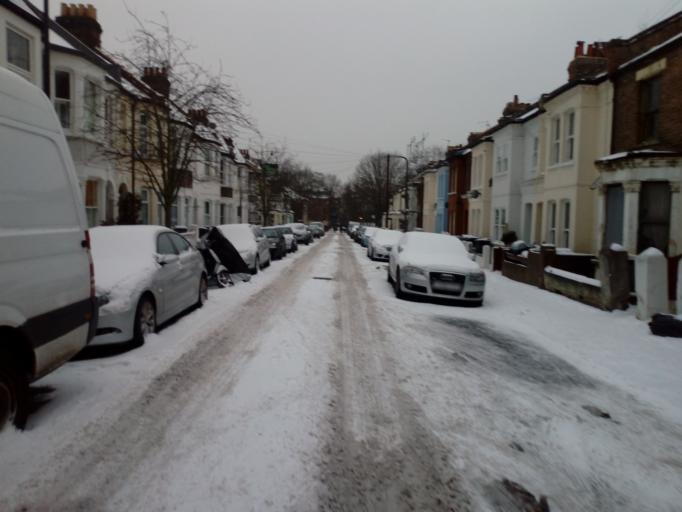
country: GB
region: England
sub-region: Greater London
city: Hammersmith
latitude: 51.5317
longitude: -0.2278
